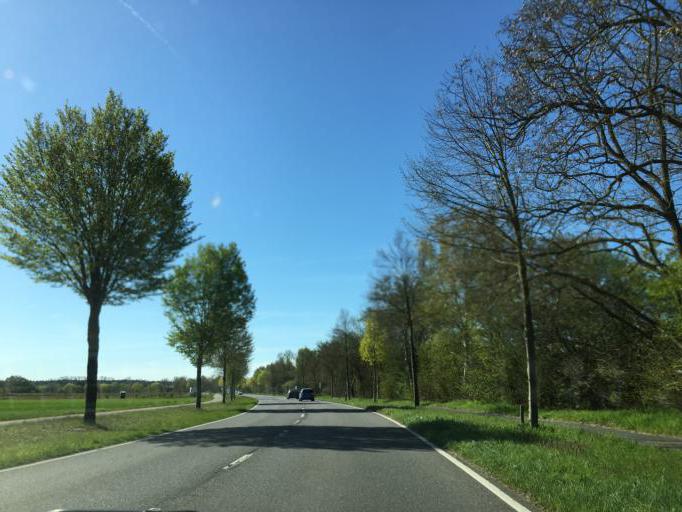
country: DE
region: Hesse
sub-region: Regierungsbezirk Darmstadt
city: Rodgau
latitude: 49.9975
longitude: 8.8527
